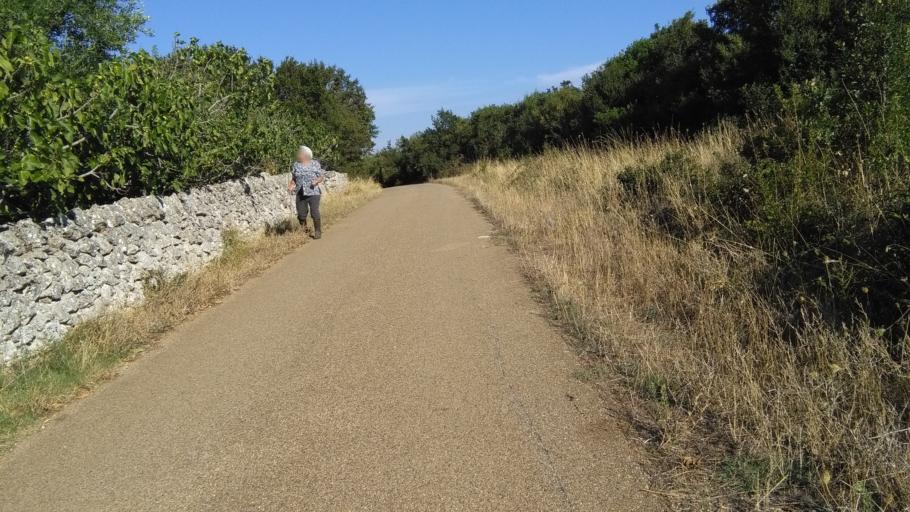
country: IT
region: Apulia
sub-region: Provincia di Bari
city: Putignano
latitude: 40.8191
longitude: 17.0524
